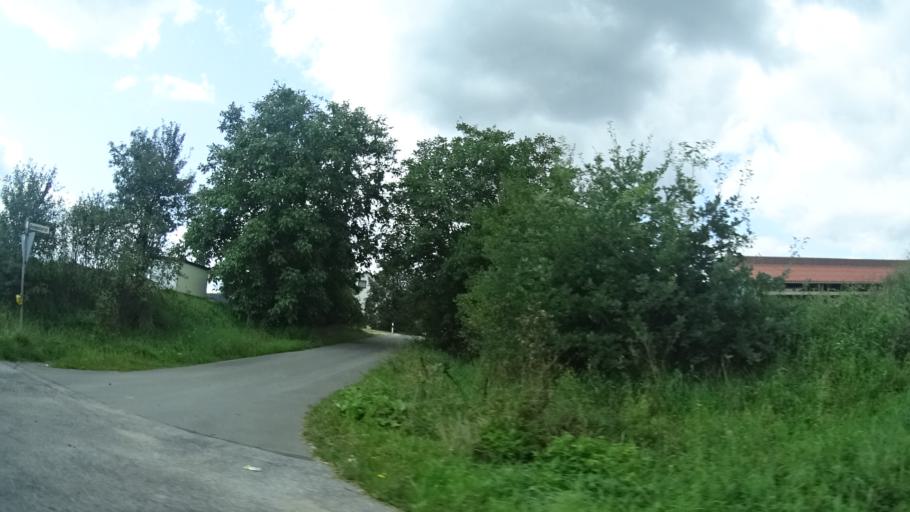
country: DE
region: Bavaria
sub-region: Upper Franconia
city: Neustadt bei Coburg
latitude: 50.3016
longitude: 11.1048
